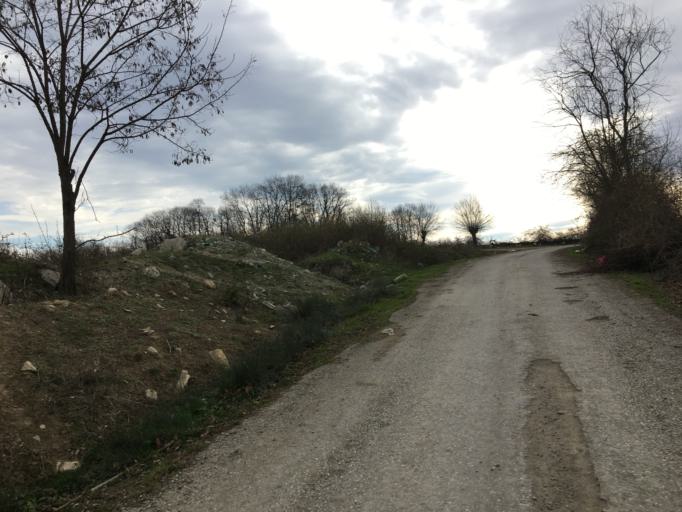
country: TR
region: Samsun
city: Alacam
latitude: 41.6003
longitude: 35.6101
